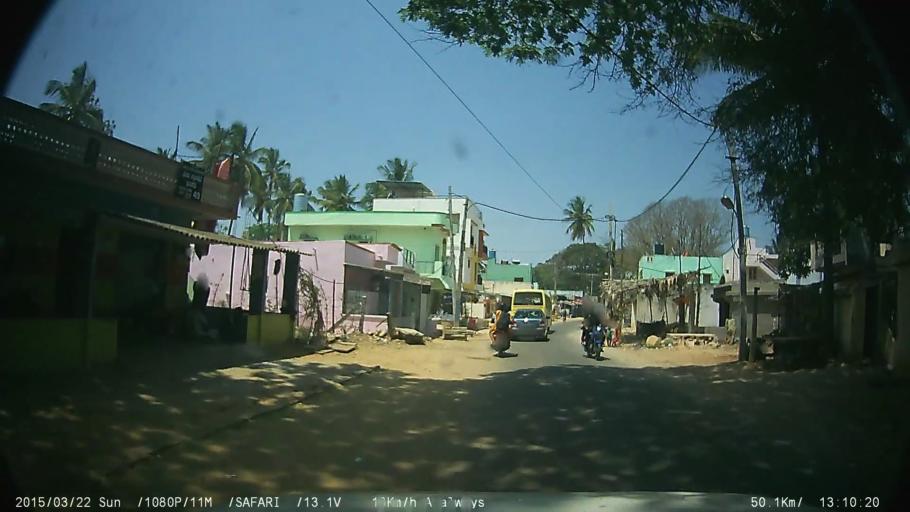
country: IN
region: Karnataka
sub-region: Bangalore Urban
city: Anekal
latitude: 12.8042
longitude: 77.5785
